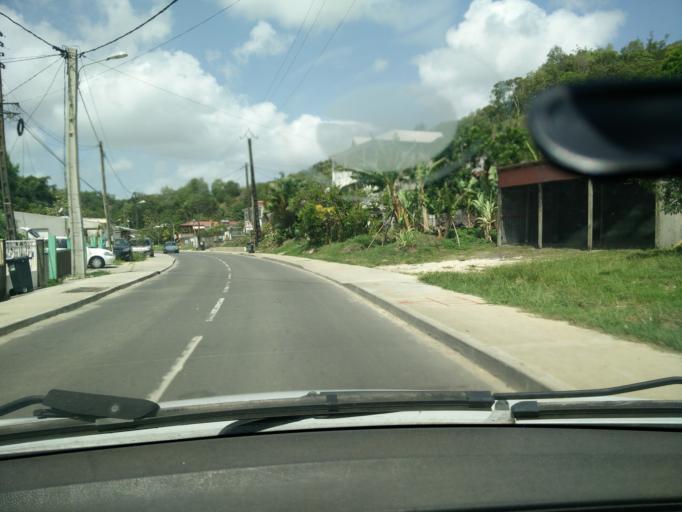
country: GP
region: Guadeloupe
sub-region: Guadeloupe
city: Les Abymes
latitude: 16.2921
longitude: -61.4636
